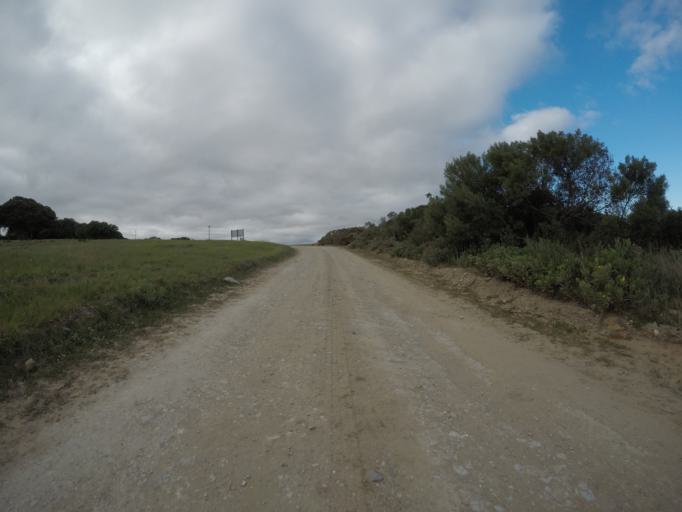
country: ZA
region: Western Cape
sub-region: Eden District Municipality
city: Riversdale
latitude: -34.4215
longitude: 21.3315
